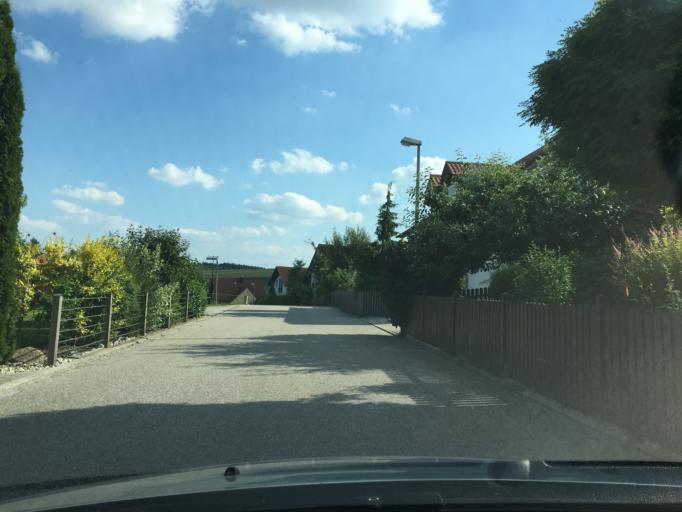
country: DE
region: Bavaria
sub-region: Lower Bavaria
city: Eching
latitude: 48.4737
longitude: 12.0426
